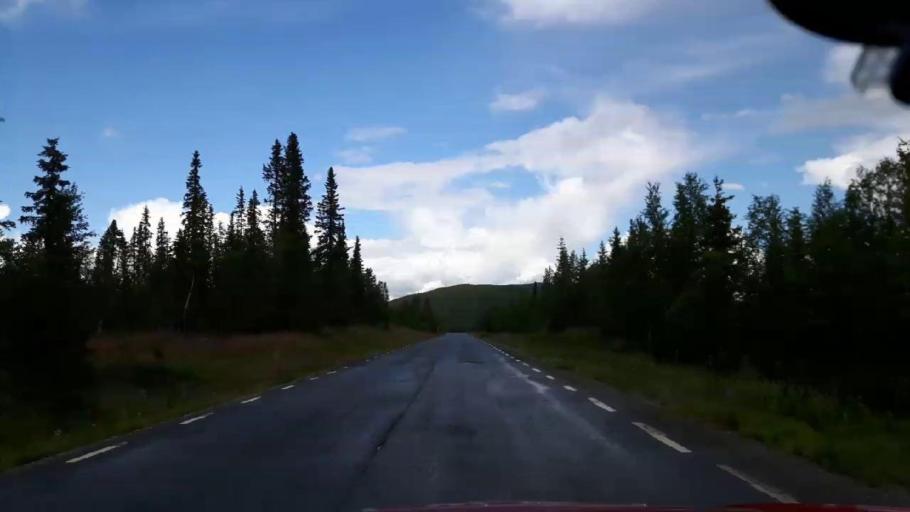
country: SE
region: Vaesterbotten
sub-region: Vilhelmina Kommun
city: Sjoberg
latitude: 65.0133
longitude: 15.1725
